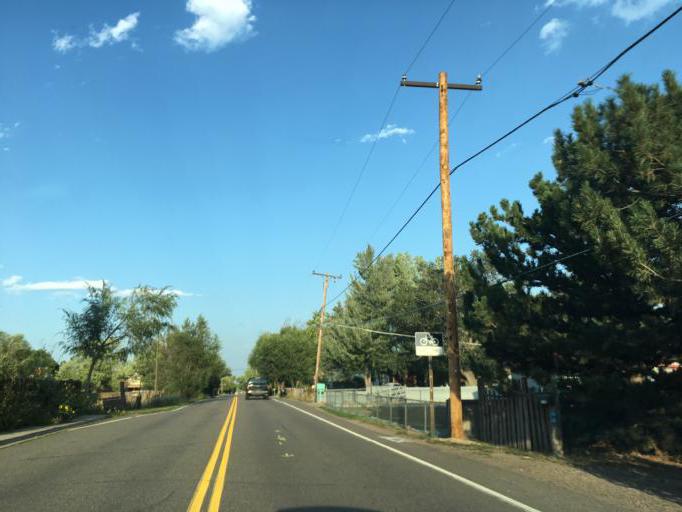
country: US
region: Colorado
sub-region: Jefferson County
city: Applewood
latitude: 39.7908
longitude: -105.1537
